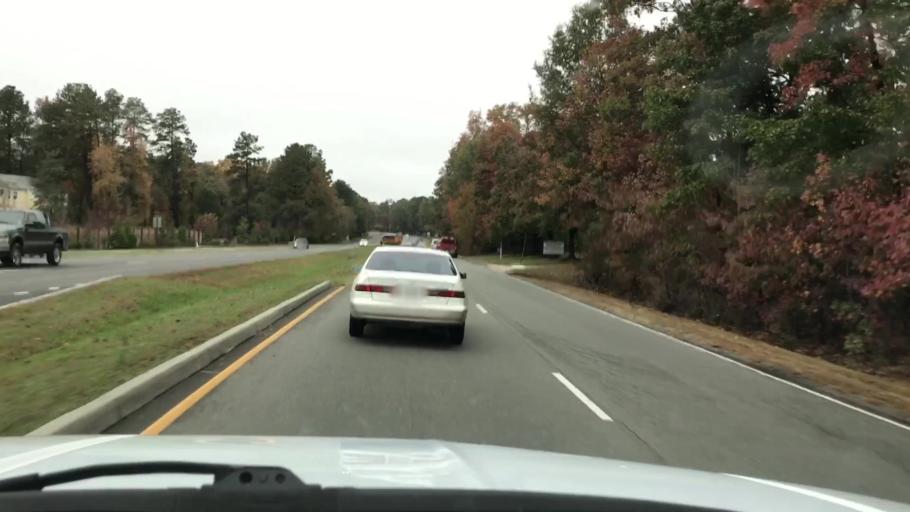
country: US
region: Virginia
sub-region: Henrico County
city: Lakeside
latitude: 37.6360
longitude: -77.4645
